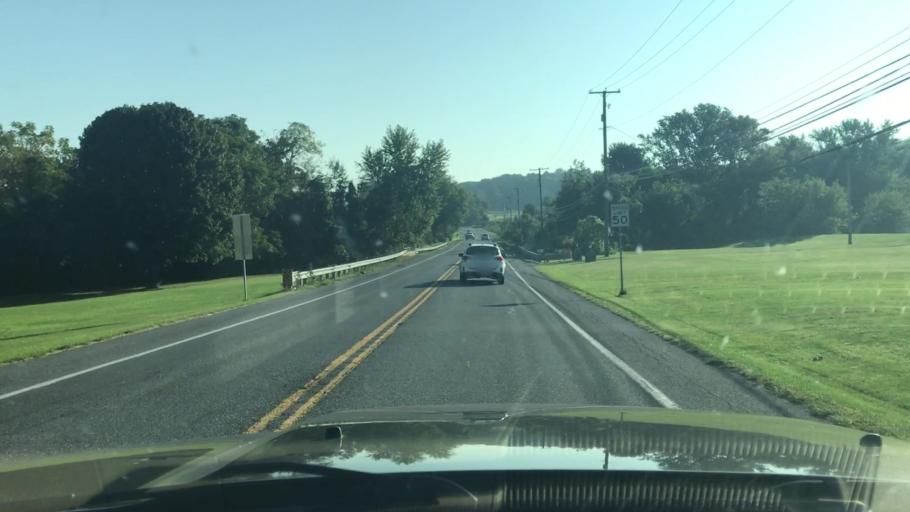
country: US
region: Pennsylvania
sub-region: Berks County
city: Topton
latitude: 40.4894
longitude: -75.7244
